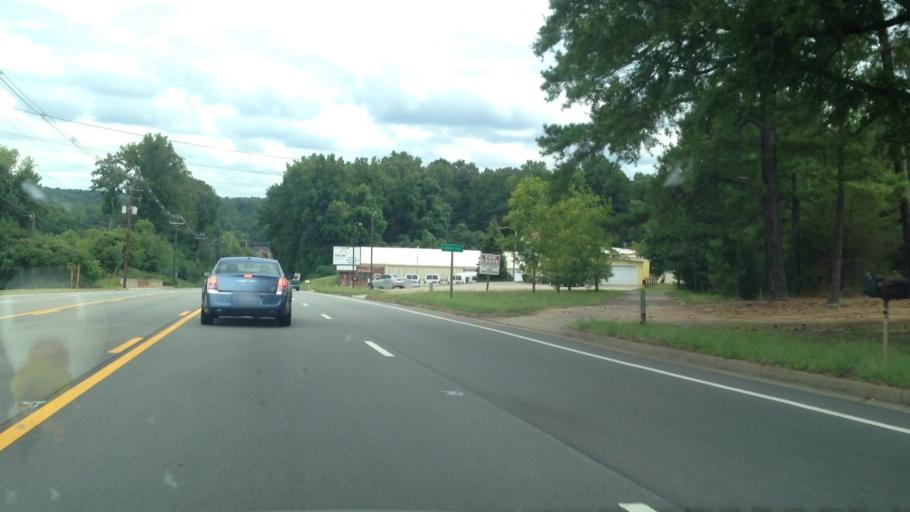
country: US
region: Virginia
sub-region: Pittsylvania County
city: Mount Hermon
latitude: 36.6436
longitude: -79.3819
